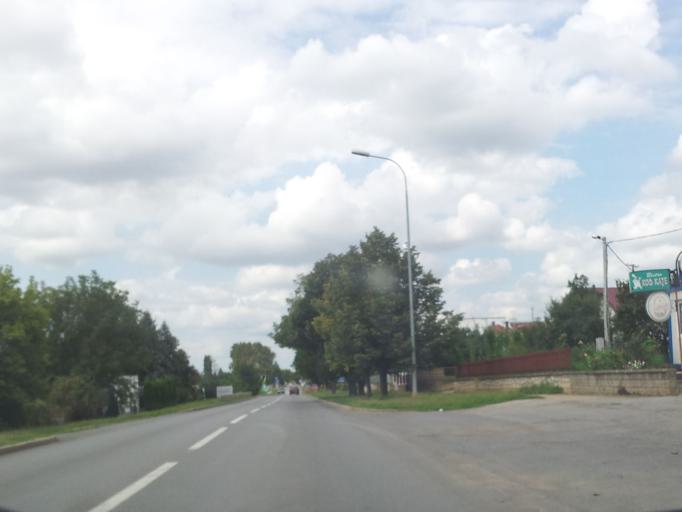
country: HR
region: Osjecko-Baranjska
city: Beli Manastir
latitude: 45.7642
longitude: 18.6220
